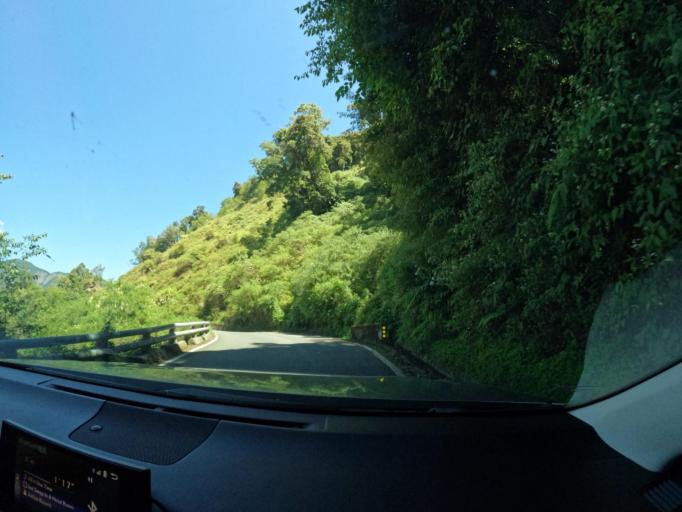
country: TW
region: Taiwan
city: Yujing
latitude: 23.2823
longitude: 120.8961
